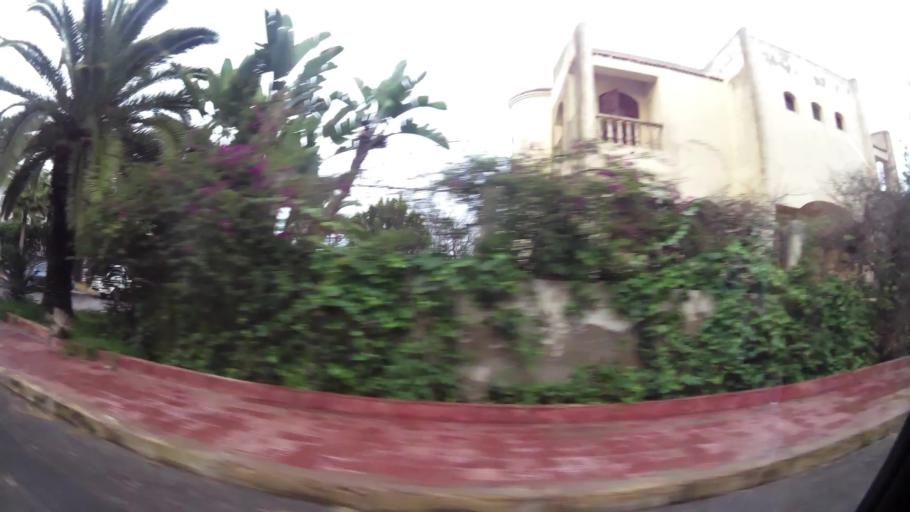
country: MA
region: Grand Casablanca
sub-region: Casablanca
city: Casablanca
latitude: 33.5804
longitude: -7.6773
